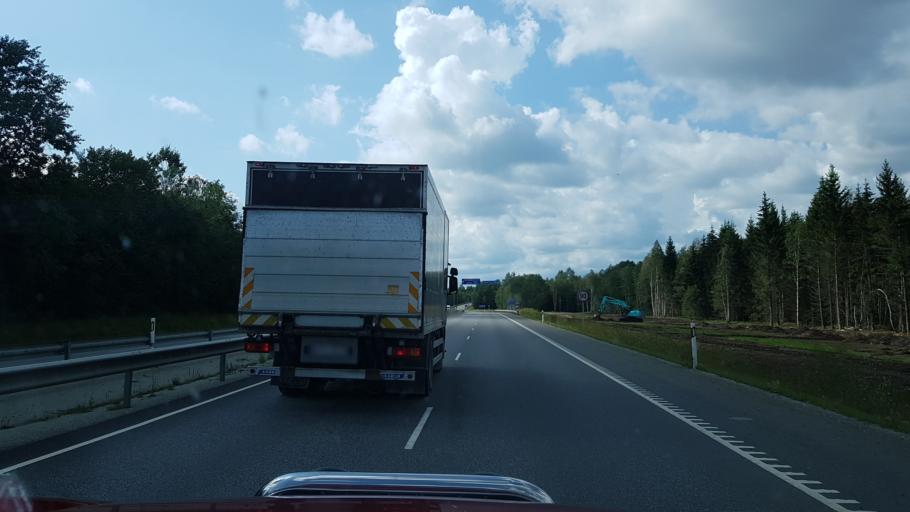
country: EE
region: Harju
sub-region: Saue linn
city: Saue
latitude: 59.3127
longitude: 24.5900
